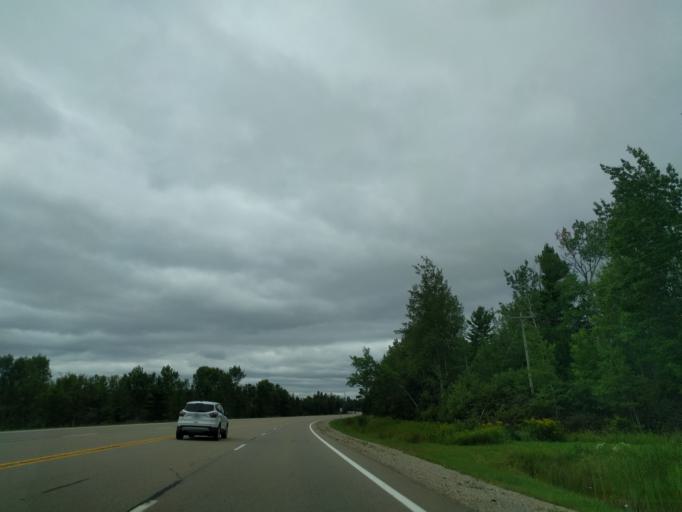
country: US
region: Michigan
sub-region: Delta County
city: Escanaba
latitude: 45.5439
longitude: -87.2739
